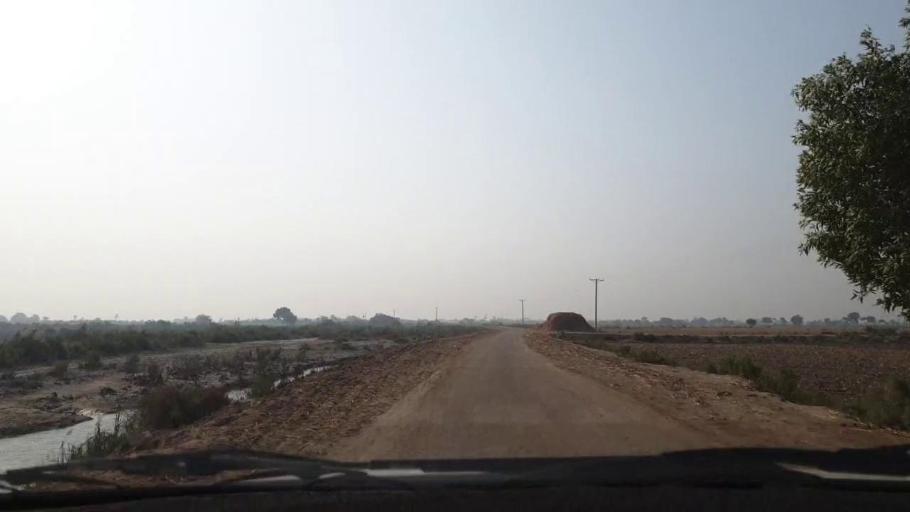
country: PK
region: Sindh
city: Tando Muhammad Khan
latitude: 25.0223
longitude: 68.4500
